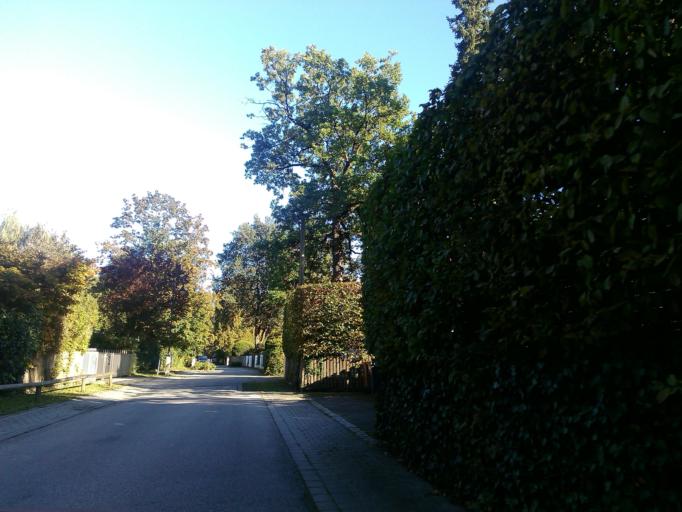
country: DE
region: Bavaria
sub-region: Upper Bavaria
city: Grafelfing
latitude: 48.1321
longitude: 11.4392
